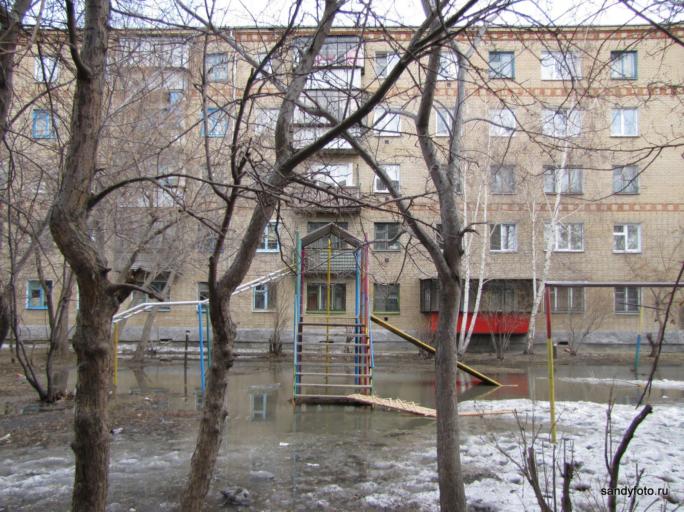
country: RU
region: Chelyabinsk
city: Troitsk
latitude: 54.1045
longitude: 61.5579
